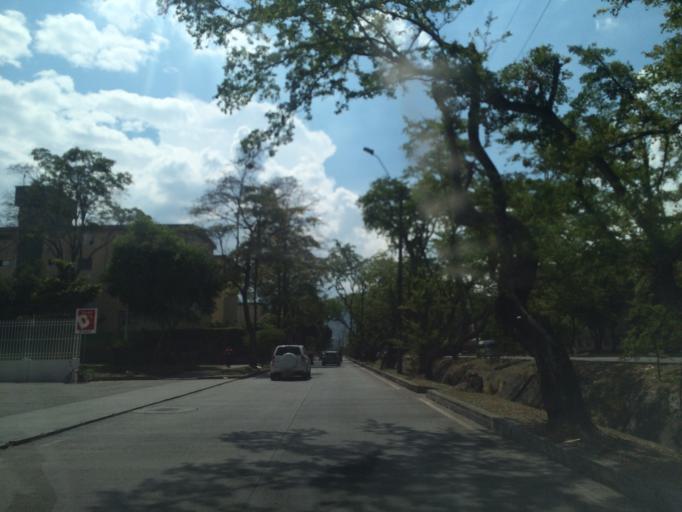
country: CO
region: Valle del Cauca
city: Cali
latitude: 3.4182
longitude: -76.5279
